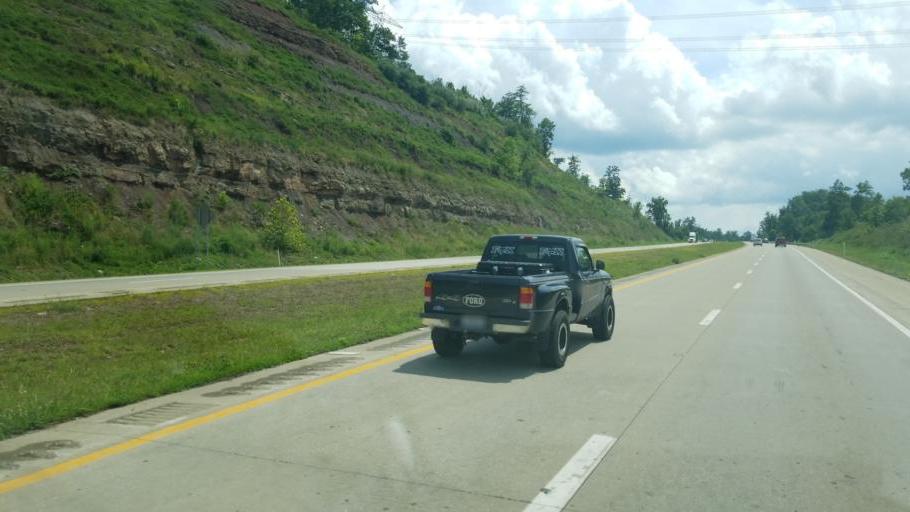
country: US
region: West Virginia
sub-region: Putnam County
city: Eleanor
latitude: 38.5107
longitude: -81.9322
